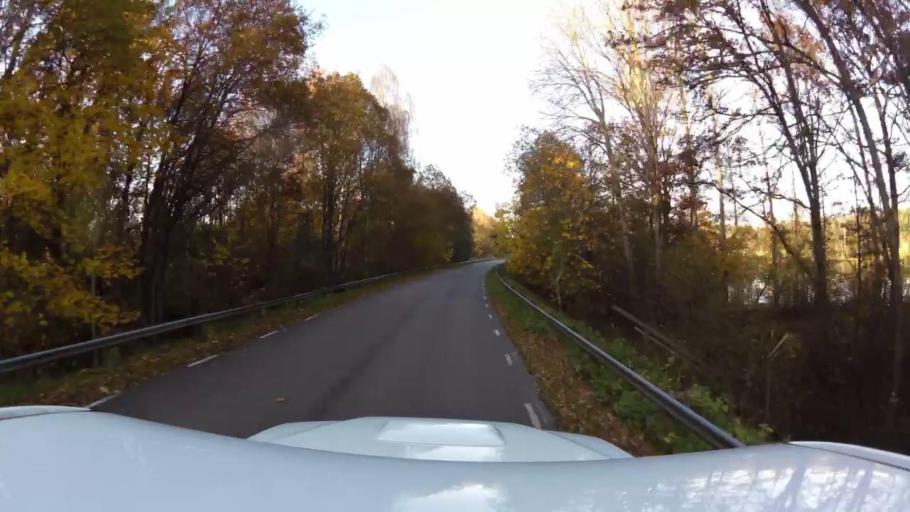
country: SE
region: OEstergoetland
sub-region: Linkopings Kommun
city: Sturefors
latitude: 58.2472
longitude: 15.6627
